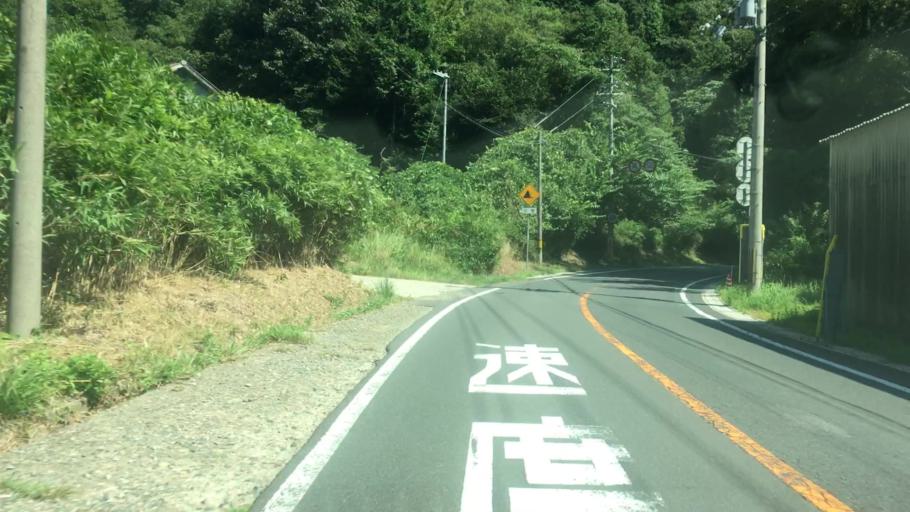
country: JP
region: Hyogo
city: Toyooka
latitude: 35.5941
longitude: 134.9125
